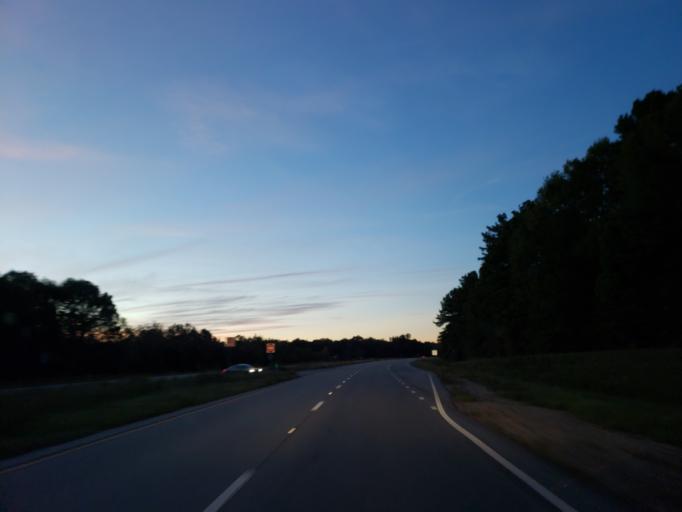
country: US
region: Mississippi
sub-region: Wayne County
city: Waynesboro
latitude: 31.8473
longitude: -88.7145
